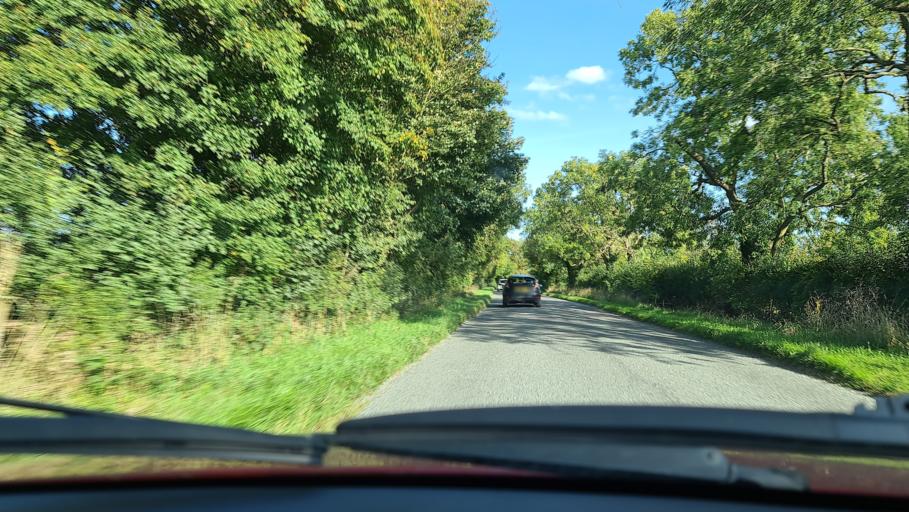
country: GB
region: England
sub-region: Northamptonshire
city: Brackley
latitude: 52.0170
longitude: -1.1927
